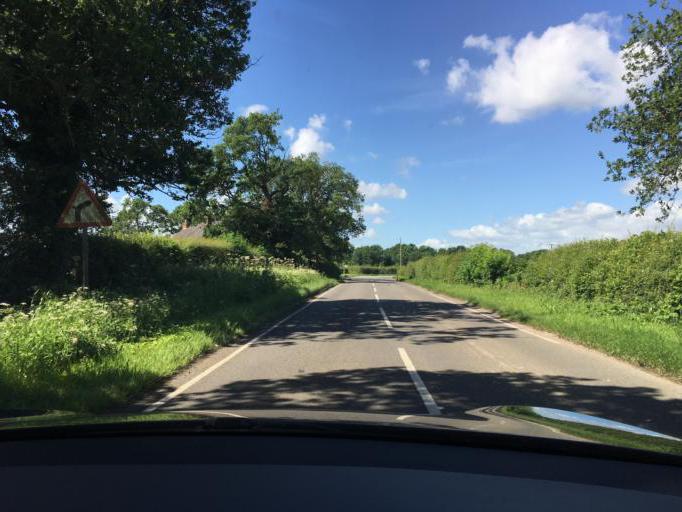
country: GB
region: England
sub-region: Cheshire East
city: Mobberley
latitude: 53.2934
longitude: -2.3097
